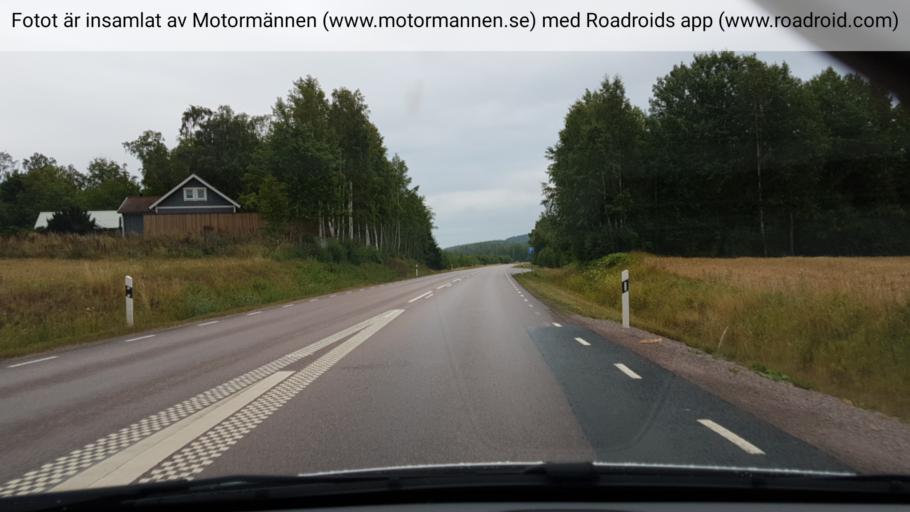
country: SE
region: Vaestra Goetaland
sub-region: Tibro Kommun
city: Tibro
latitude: 58.4556
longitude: 14.2267
